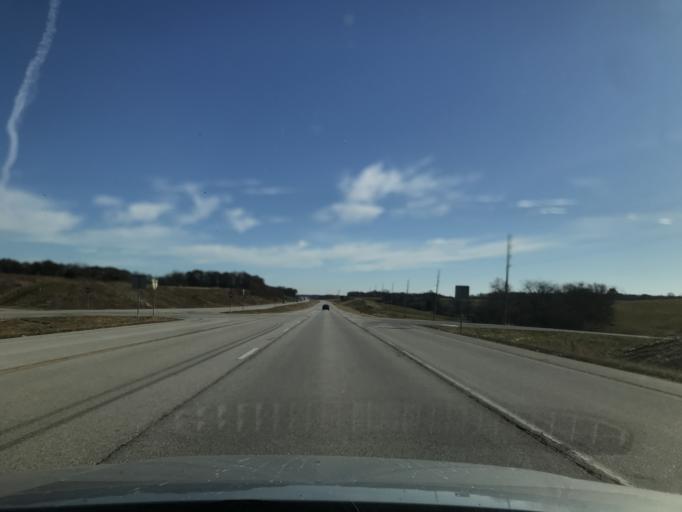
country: US
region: Illinois
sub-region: Hancock County
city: Carthage
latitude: 40.4145
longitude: -91.0351
